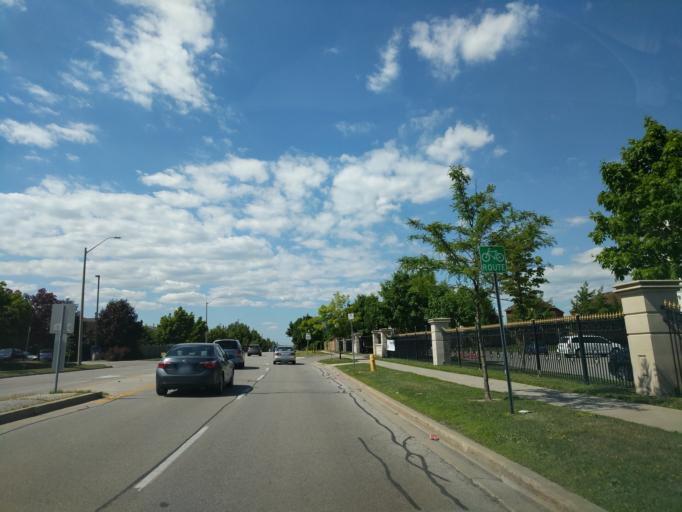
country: CA
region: Ontario
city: Markham
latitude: 43.8417
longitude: -79.2650
